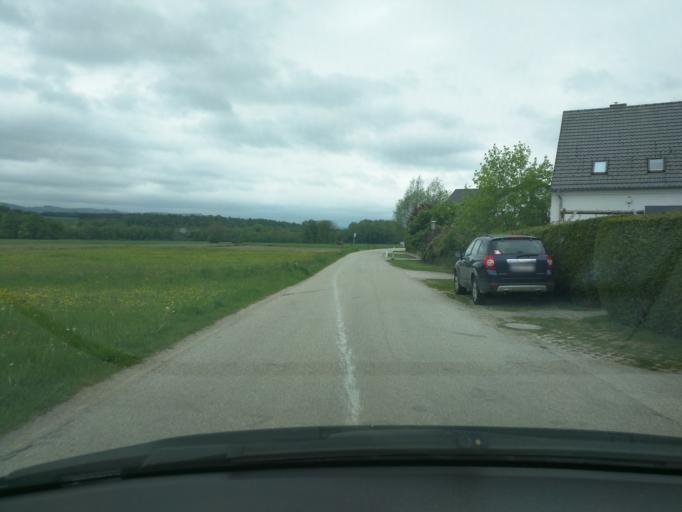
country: AT
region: Lower Austria
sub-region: Politischer Bezirk Amstetten
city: Sankt Georgen am Ybbsfelde
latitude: 48.1077
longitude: 14.9476
